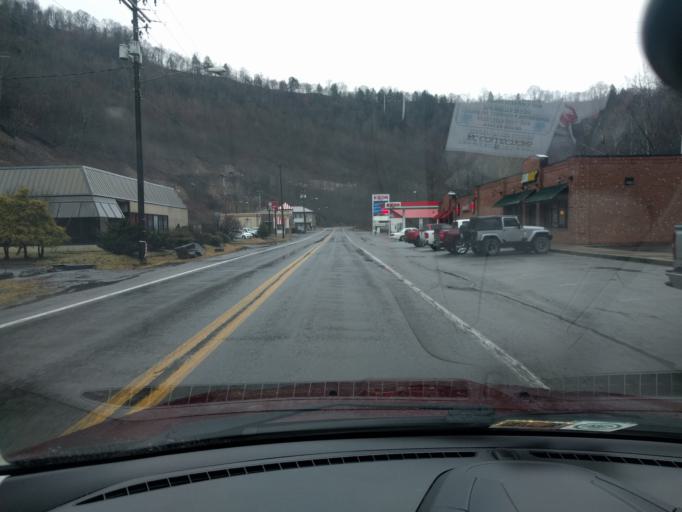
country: US
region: West Virginia
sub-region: McDowell County
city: Welch
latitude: 37.4301
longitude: -81.5548
